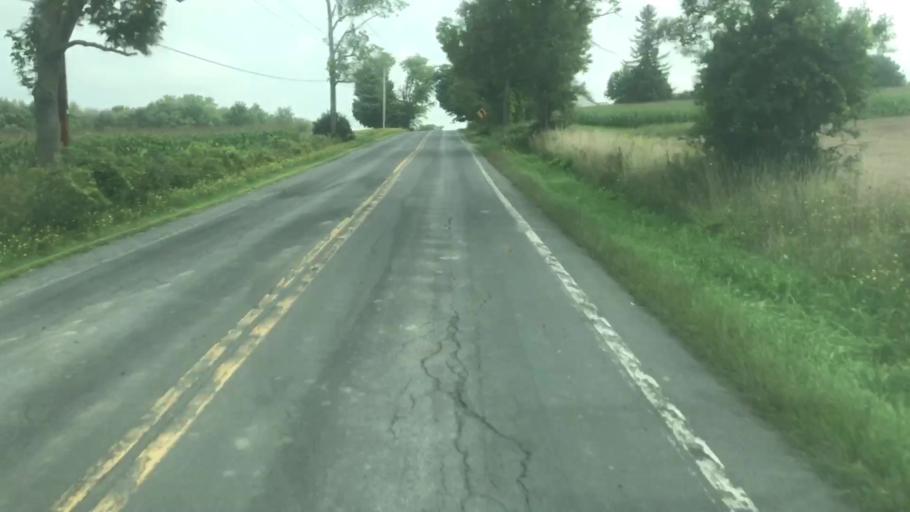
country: US
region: New York
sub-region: Onondaga County
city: Skaneateles
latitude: 42.8716
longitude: -76.4470
